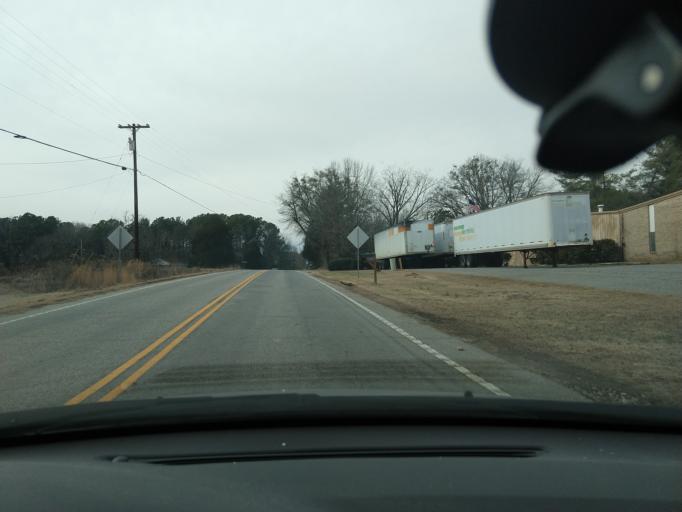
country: US
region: South Carolina
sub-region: Spartanburg County
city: Cowpens
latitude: 35.0089
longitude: -81.8548
